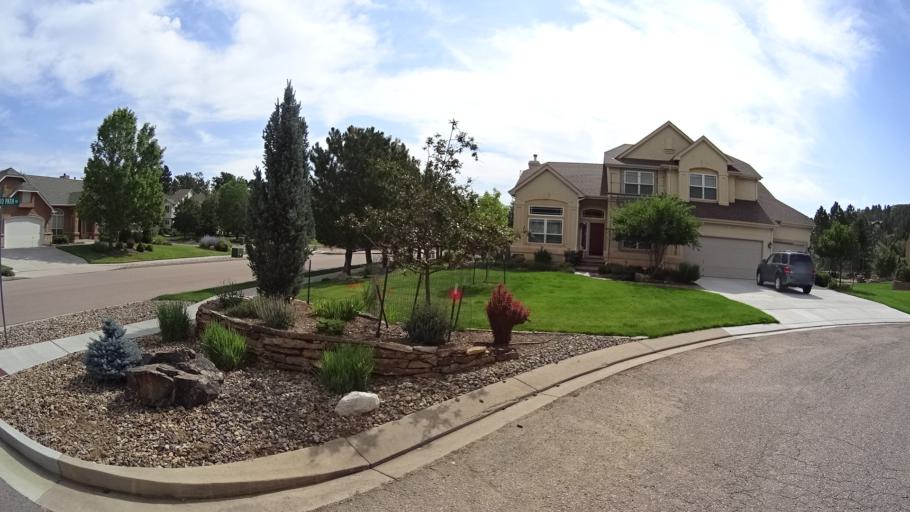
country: US
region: Colorado
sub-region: El Paso County
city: Air Force Academy
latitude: 38.9427
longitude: -104.8665
